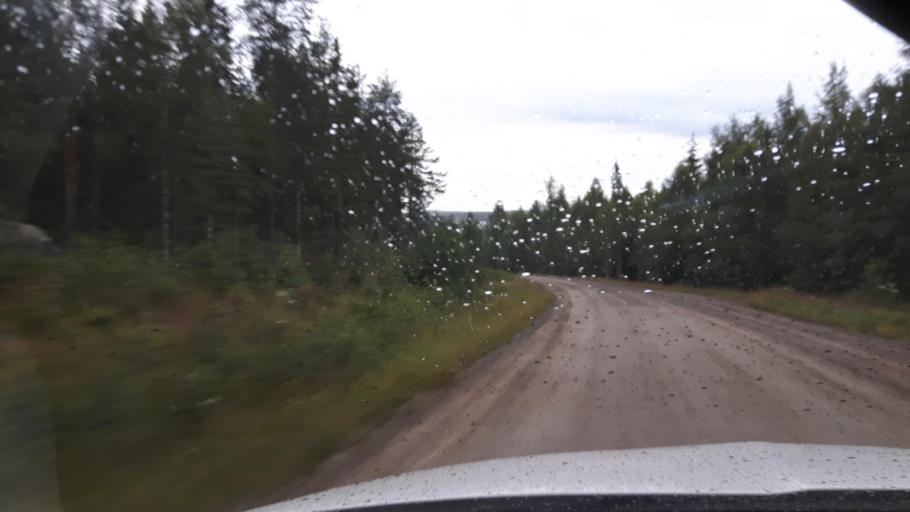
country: SE
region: Gaevleborg
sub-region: Ljusdals Kommun
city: Farila
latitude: 62.0099
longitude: 15.8362
